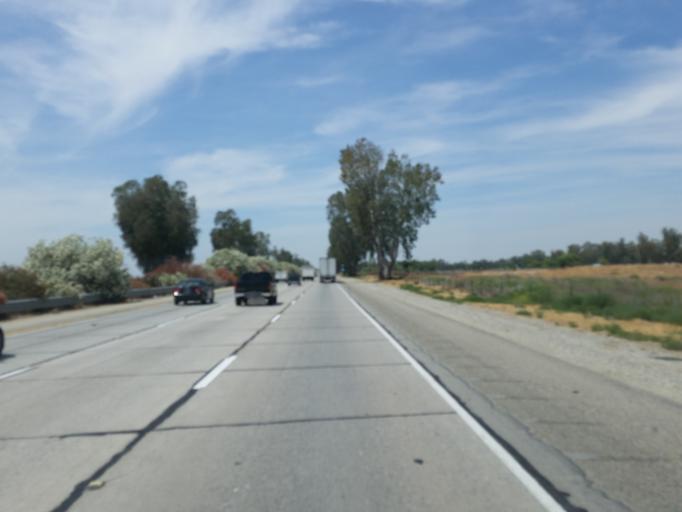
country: US
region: California
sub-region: Kern County
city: Greenfield
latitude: 35.1824
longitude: -119.0060
